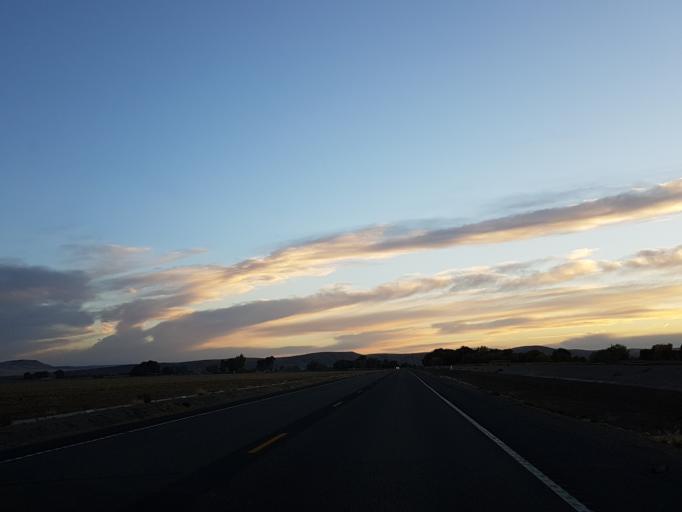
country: US
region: Oregon
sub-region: Malheur County
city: Vale
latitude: 43.9449
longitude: -117.3012
